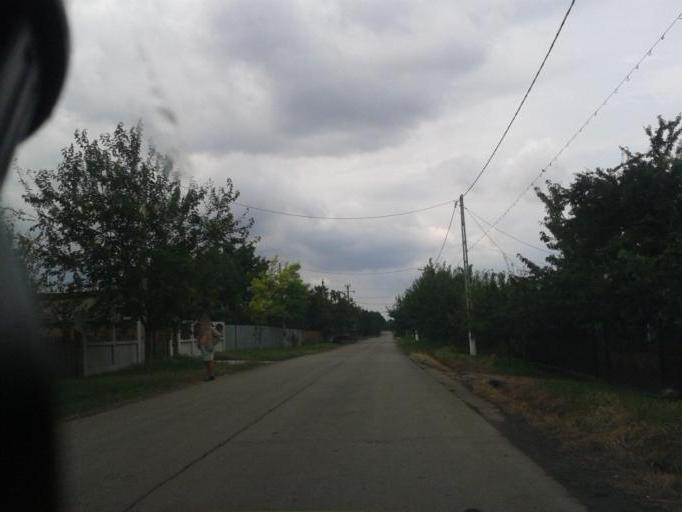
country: RO
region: Calarasi
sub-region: Comuna Fundulea
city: Fundulea
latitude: 44.5044
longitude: 26.4952
